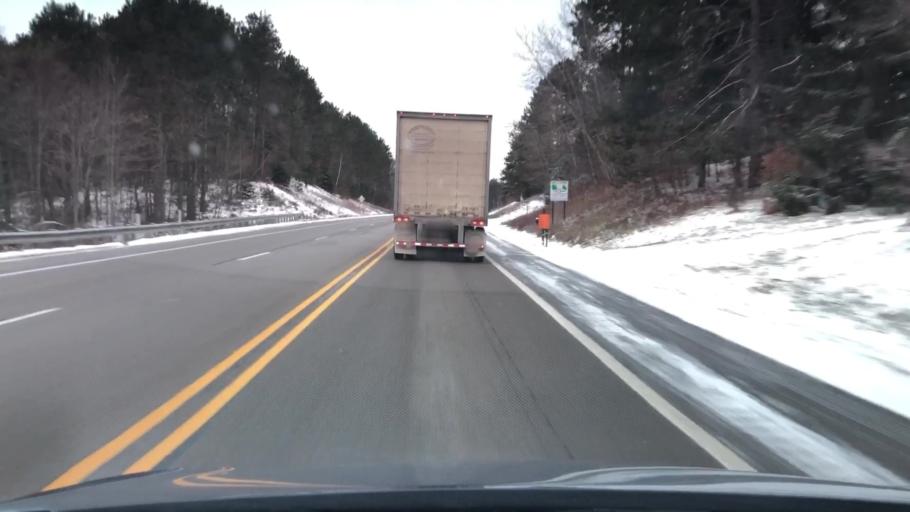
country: US
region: Michigan
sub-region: Wexford County
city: Cadillac
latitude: 44.1803
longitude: -85.3813
